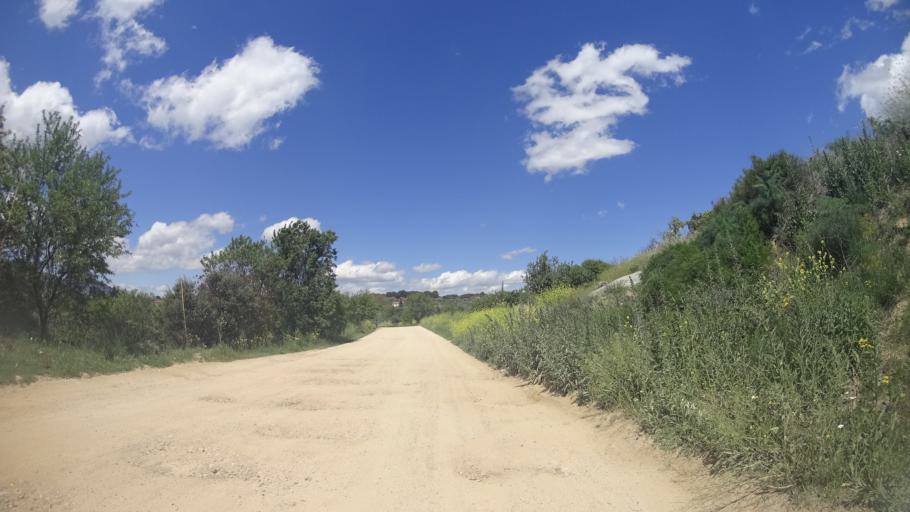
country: ES
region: Madrid
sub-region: Provincia de Madrid
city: San Martin de Valdeiglesias
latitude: 40.3650
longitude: -4.3862
